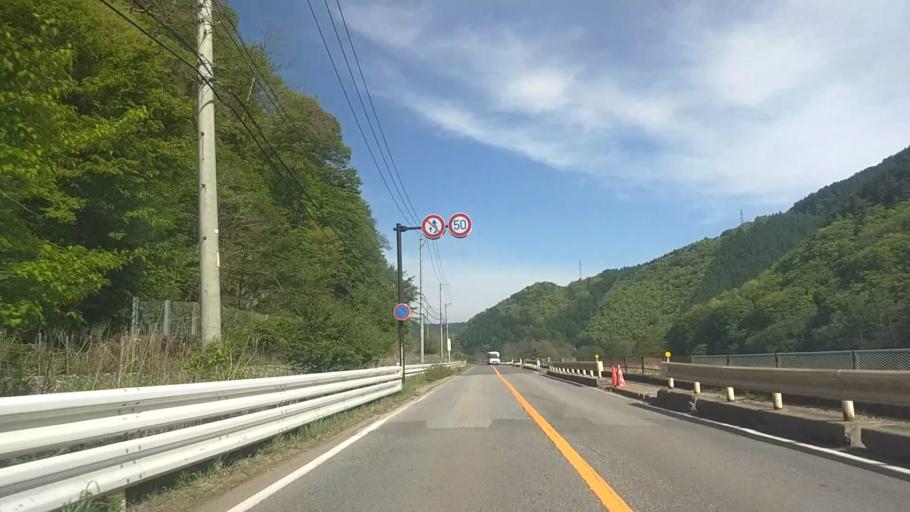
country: JP
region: Nagano
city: Saku
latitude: 36.0319
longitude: 138.4847
